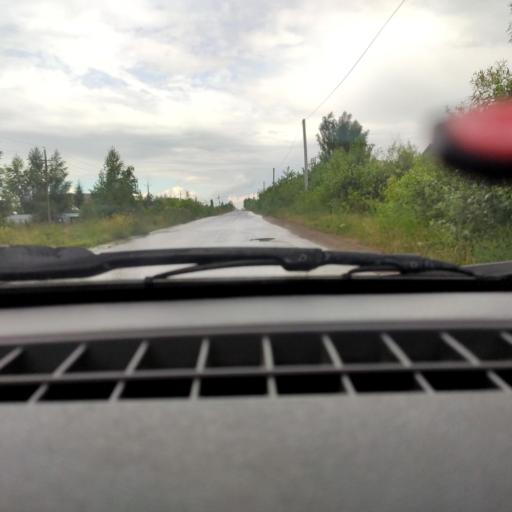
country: RU
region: Bashkortostan
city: Kabakovo
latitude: 54.5693
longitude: 56.2722
